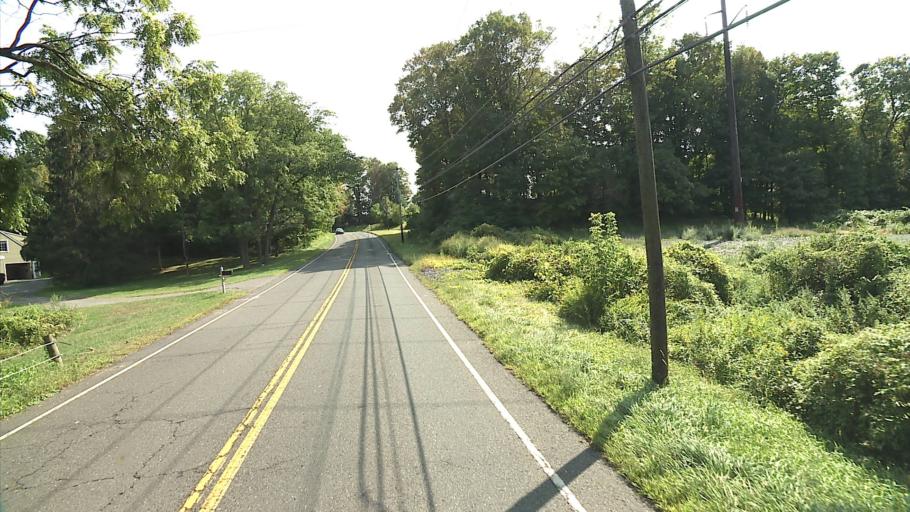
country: US
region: Connecticut
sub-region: New Haven County
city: Heritage Village
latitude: 41.4813
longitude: -73.2572
